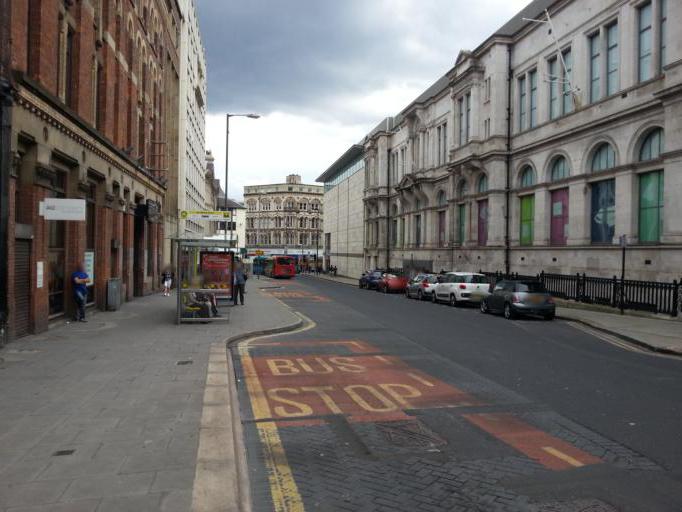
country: GB
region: England
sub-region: Liverpool
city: Liverpool
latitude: 53.4075
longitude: -2.9857
